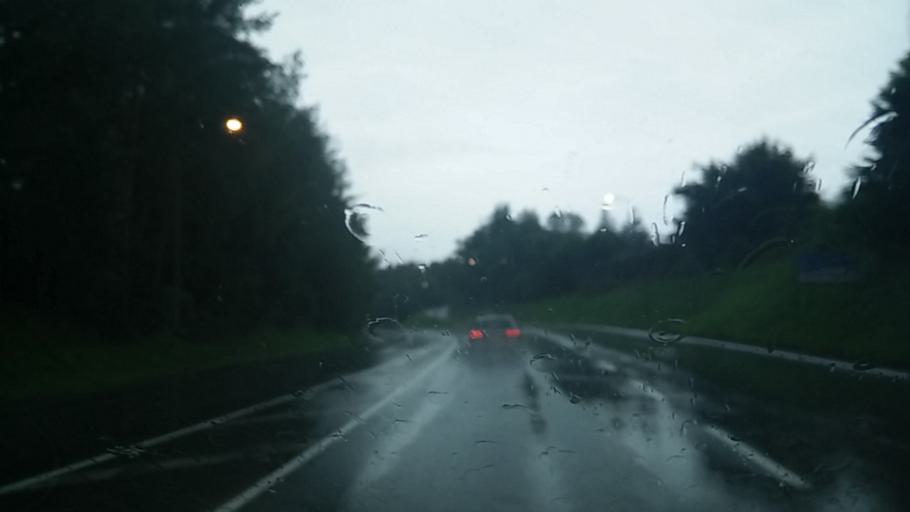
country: AT
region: Carinthia
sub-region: Villach Stadt
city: Villach
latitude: 46.6257
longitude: 13.8694
